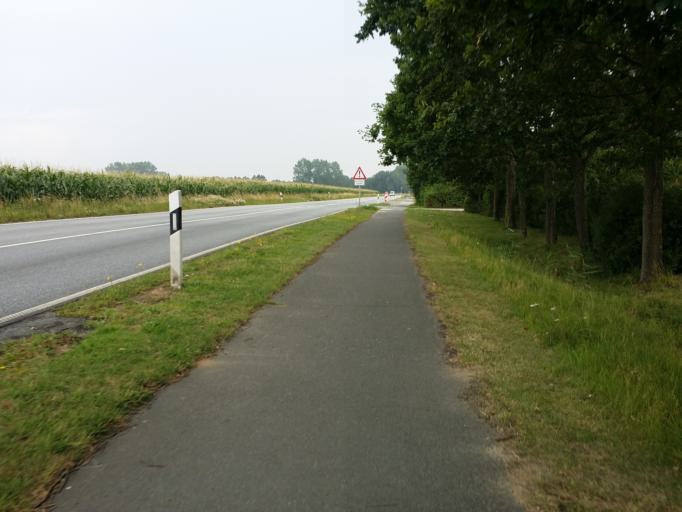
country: DE
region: Schleswig-Holstein
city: Blomesche Wildnis
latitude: 53.8113
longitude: 9.4257
